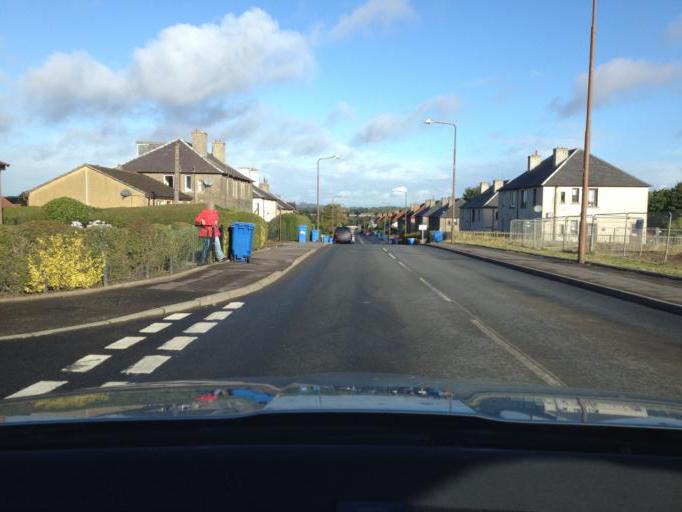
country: GB
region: Scotland
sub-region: West Lothian
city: East Calder
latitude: 55.8903
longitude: -3.4620
